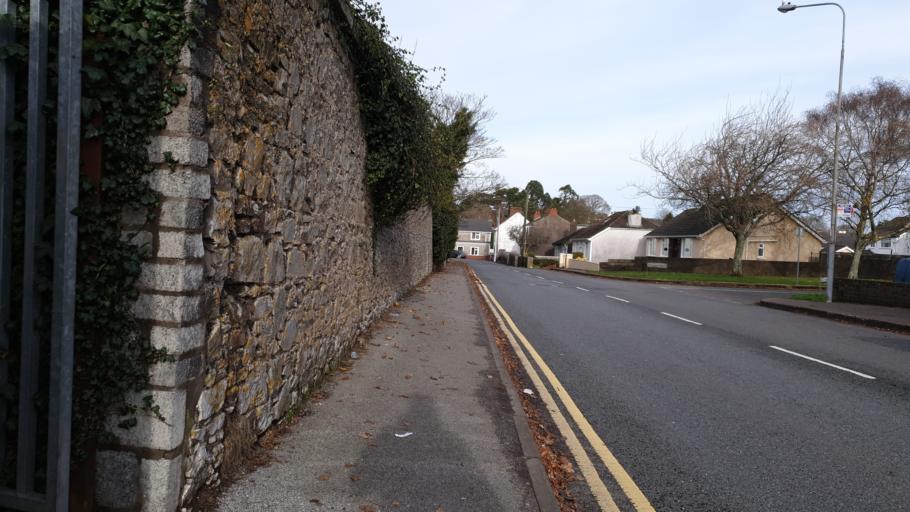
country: IE
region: Munster
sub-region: County Cork
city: Cork
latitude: 51.8952
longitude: -8.4103
